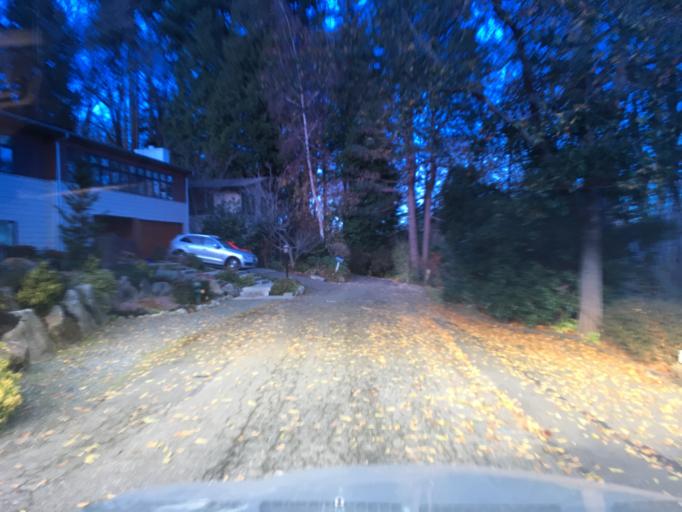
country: US
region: Washington
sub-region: King County
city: Inglewood-Finn Hill
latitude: 47.6862
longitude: -122.2673
